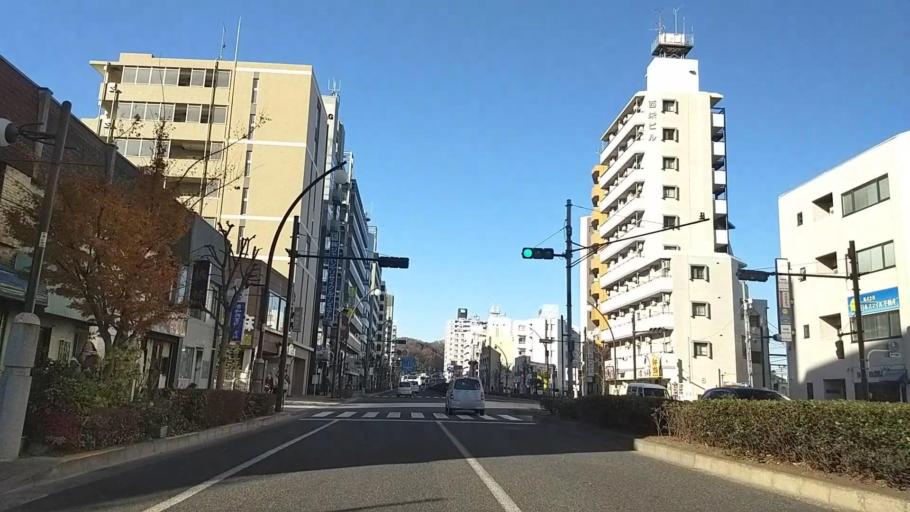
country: JP
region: Tokyo
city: Hino
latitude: 35.6507
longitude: 139.4434
